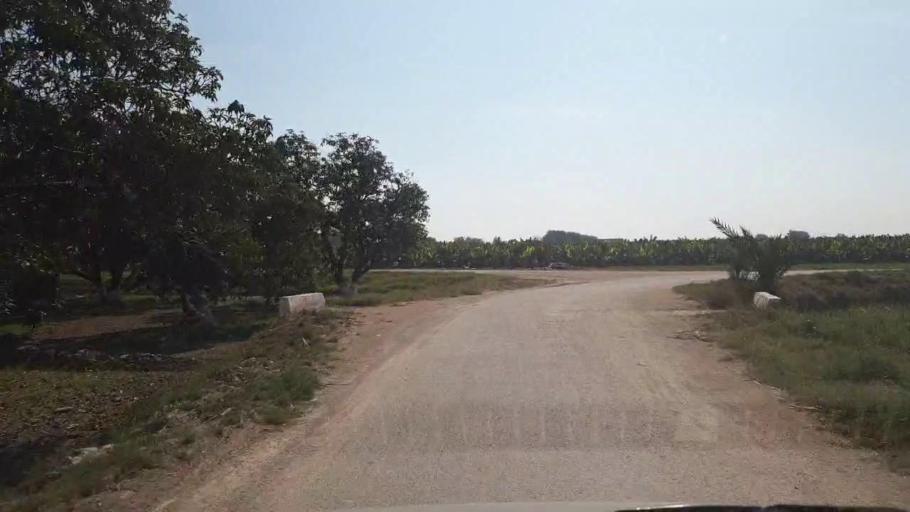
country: PK
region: Sindh
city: Chambar
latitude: 25.3783
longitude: 68.8071
